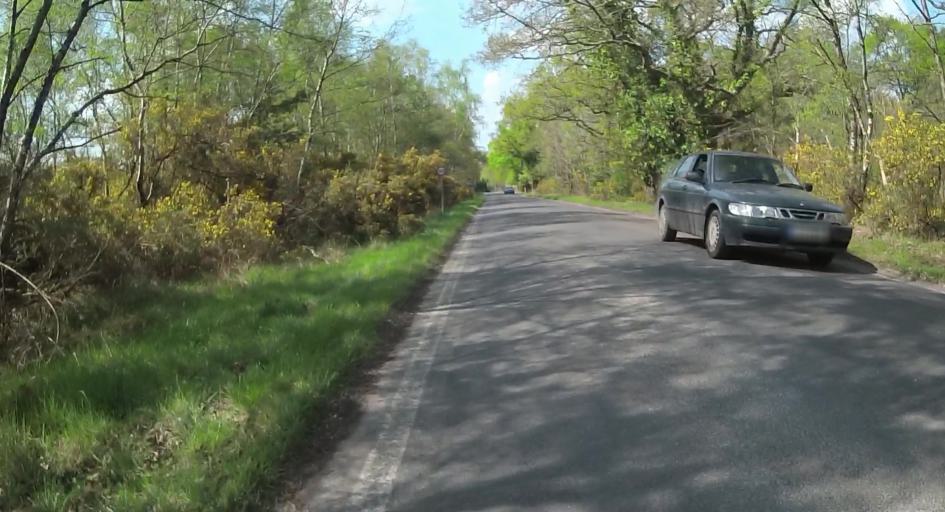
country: GB
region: England
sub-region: Hampshire
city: Tadley
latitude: 51.3570
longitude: -1.1049
